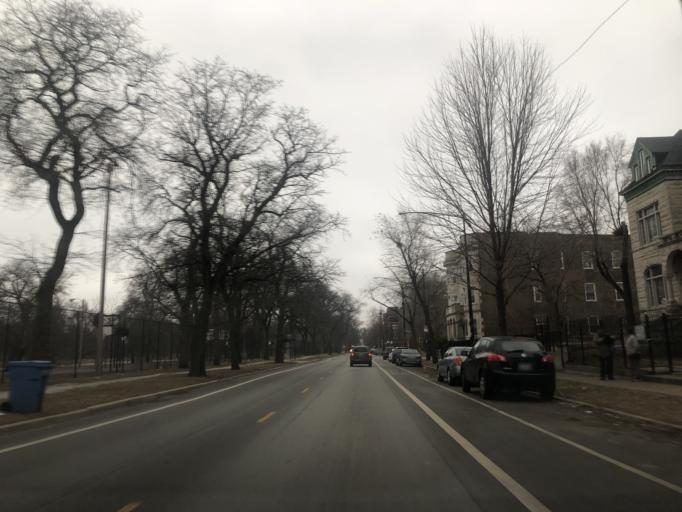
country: US
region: Illinois
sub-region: Cook County
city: Chicago
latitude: 41.7920
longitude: -87.6159
